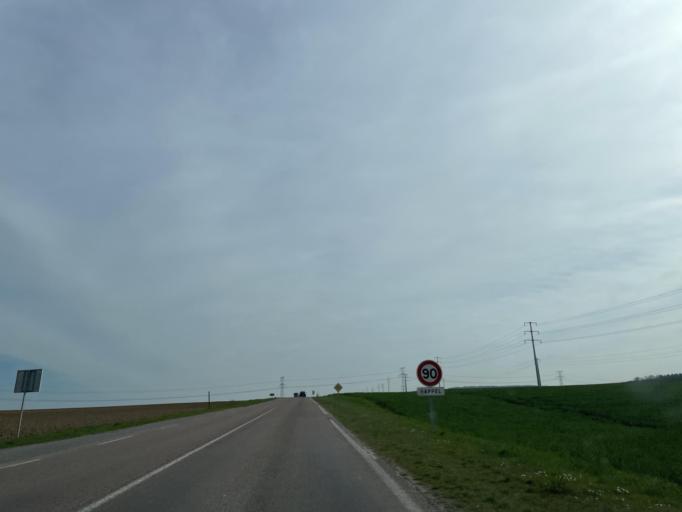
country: FR
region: Champagne-Ardenne
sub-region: Departement de l'Aube
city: Nogent-sur-Seine
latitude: 48.4963
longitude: 3.5348
